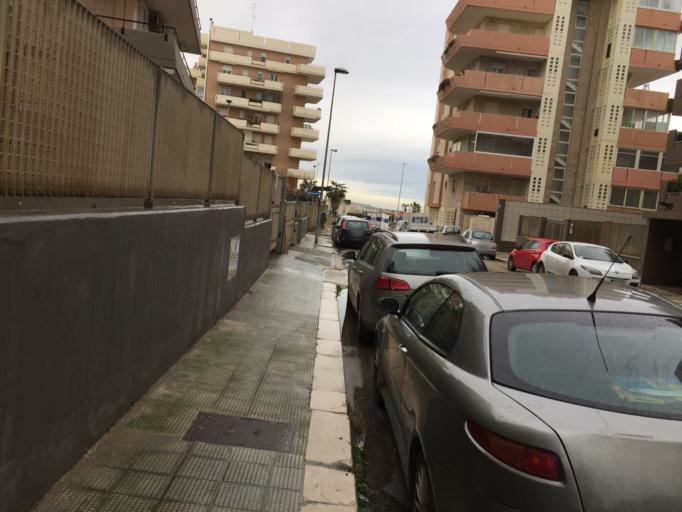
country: IT
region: Apulia
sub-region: Provincia di Bari
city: Bari
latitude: 41.1384
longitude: 16.8432
